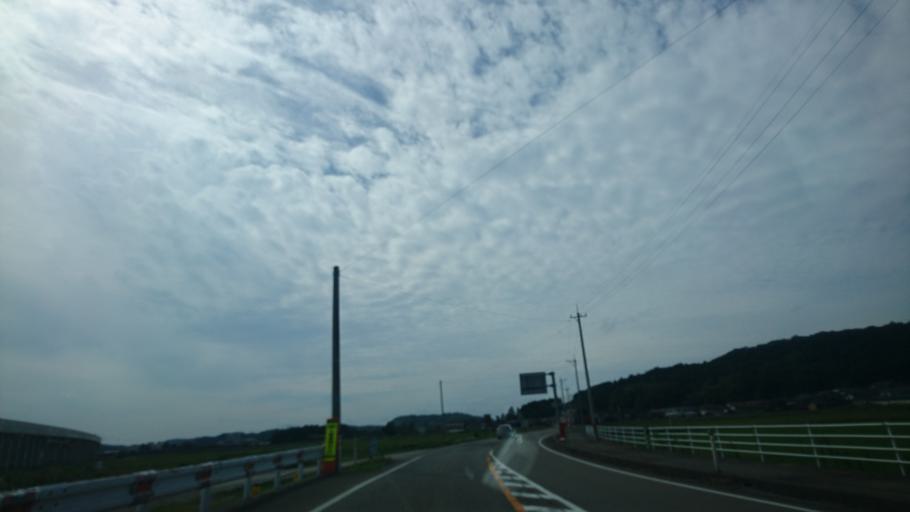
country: JP
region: Ishikawa
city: Komatsu
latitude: 36.3146
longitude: 136.3322
